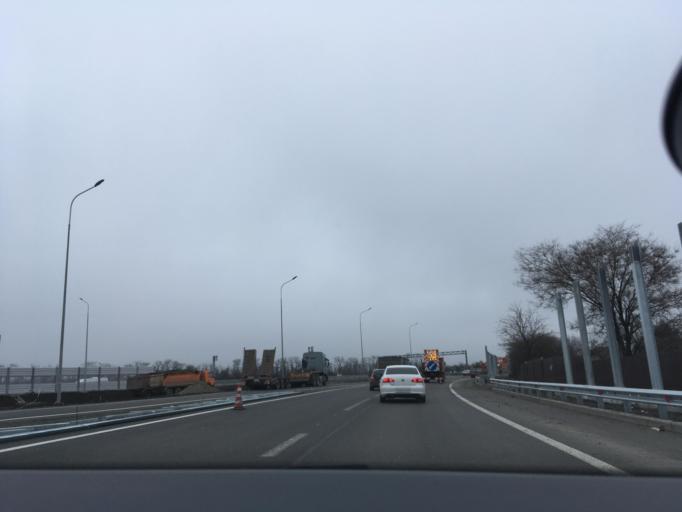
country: RU
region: Rostov
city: Bataysk
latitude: 47.0798
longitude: 39.7680
